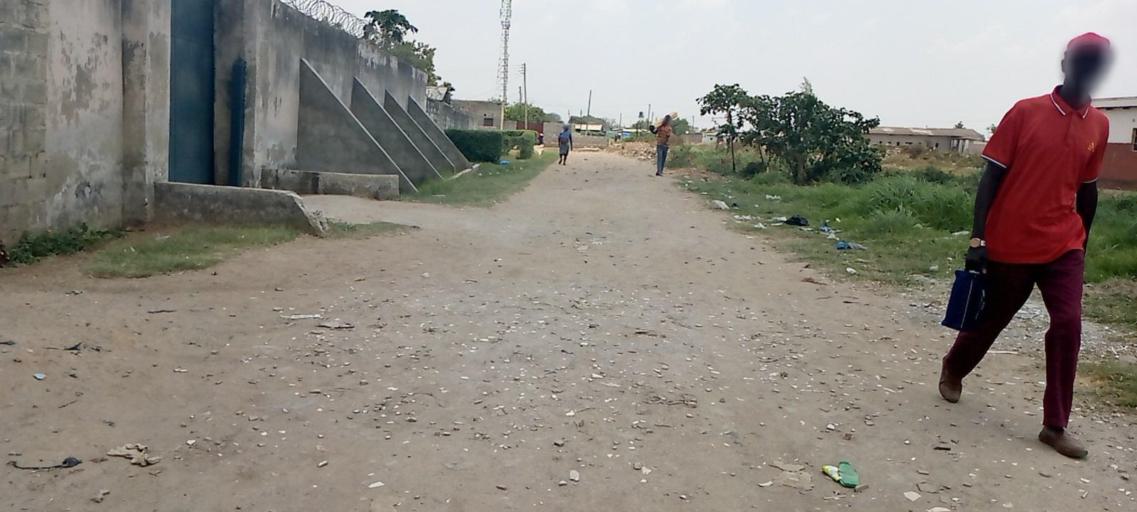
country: ZM
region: Lusaka
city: Lusaka
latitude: -15.4011
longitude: 28.3449
